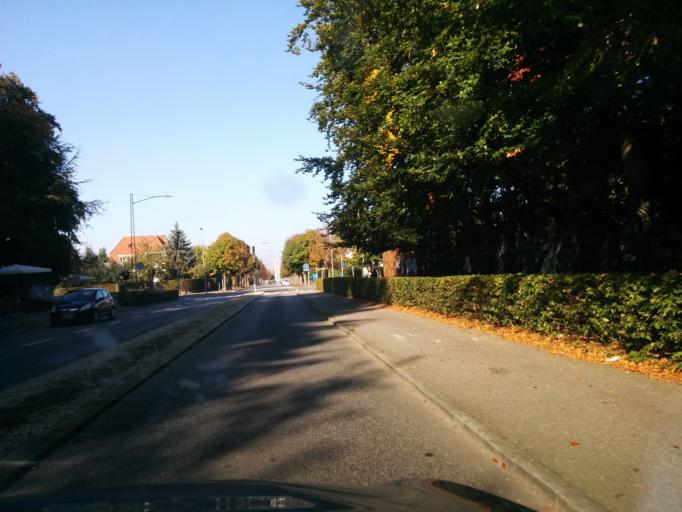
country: DK
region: Central Jutland
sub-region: Arhus Kommune
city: Arhus
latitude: 56.1366
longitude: 10.1956
